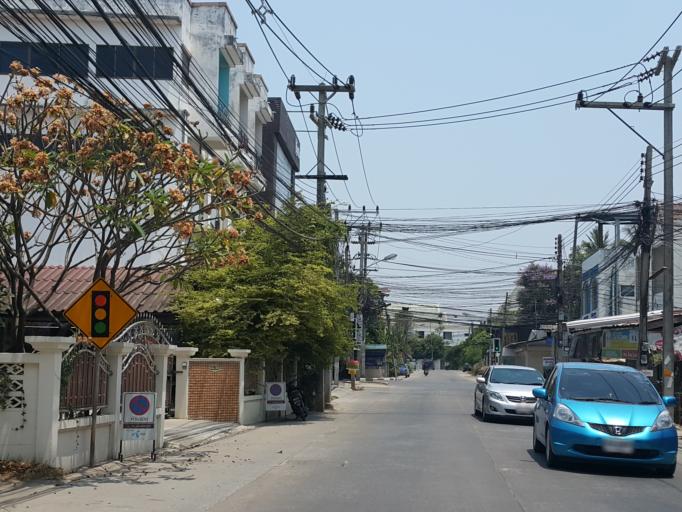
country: TH
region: Phitsanulok
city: Phitsanulok
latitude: 16.8152
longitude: 100.2566
